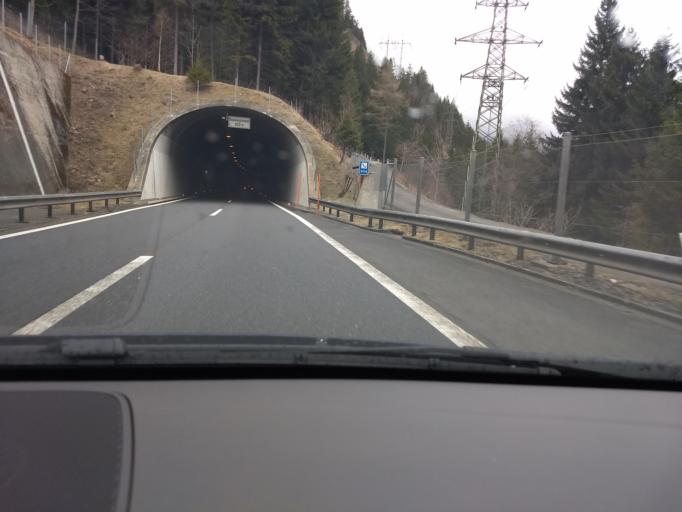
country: CH
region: Uri
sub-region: Uri
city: Andermatt
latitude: 46.6827
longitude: 8.5921
